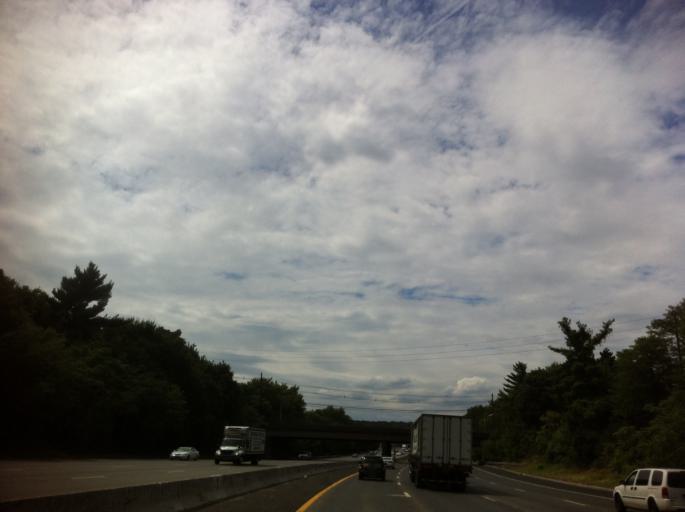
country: US
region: New Jersey
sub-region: Bergen County
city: Elmwood Park
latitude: 40.9014
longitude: -74.1290
